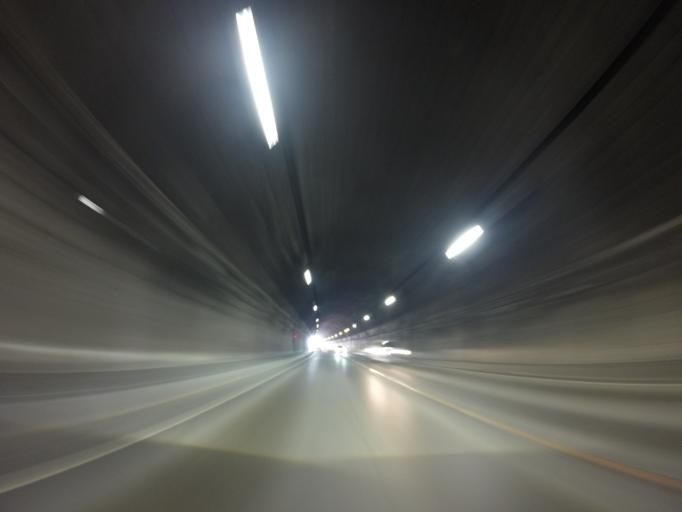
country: JP
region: Shizuoka
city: Mishima
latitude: 35.0658
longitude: 138.9243
